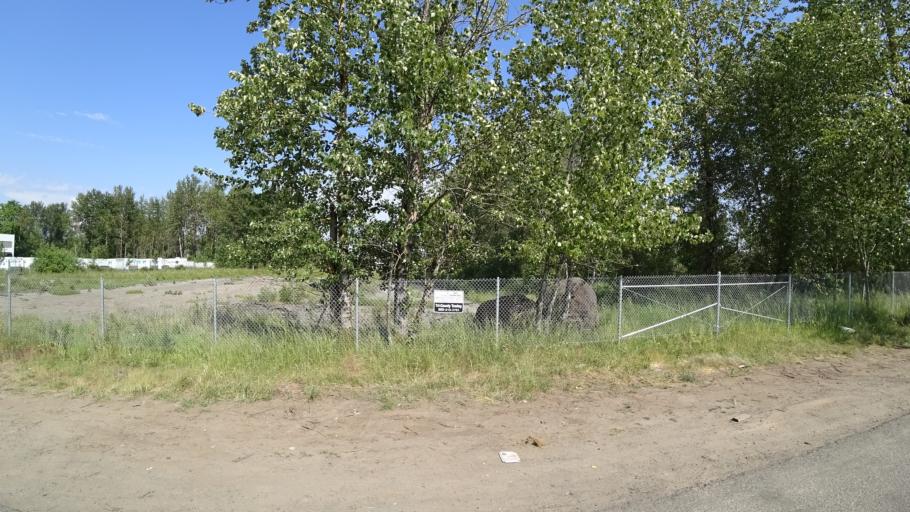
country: US
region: Oregon
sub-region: Multnomah County
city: Fairview
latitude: 45.5553
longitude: -122.5157
